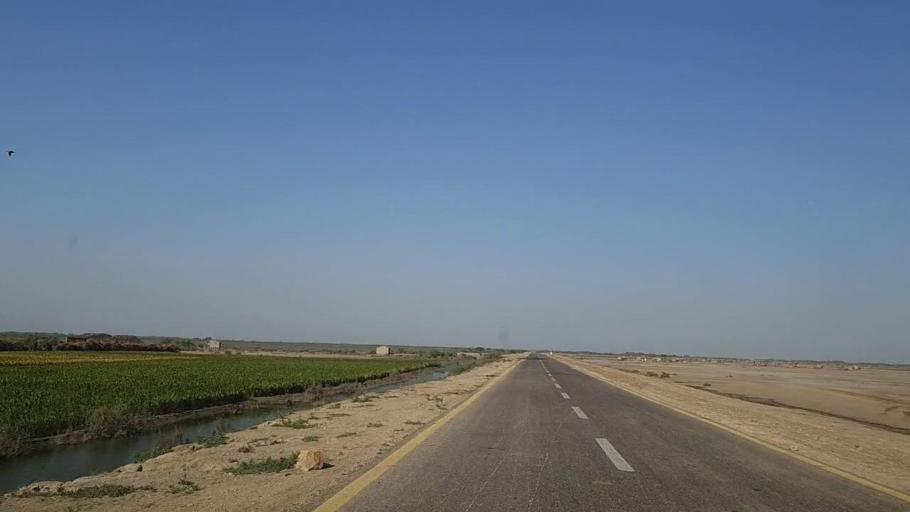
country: PK
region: Sindh
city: Jati
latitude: 24.4361
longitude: 68.3165
